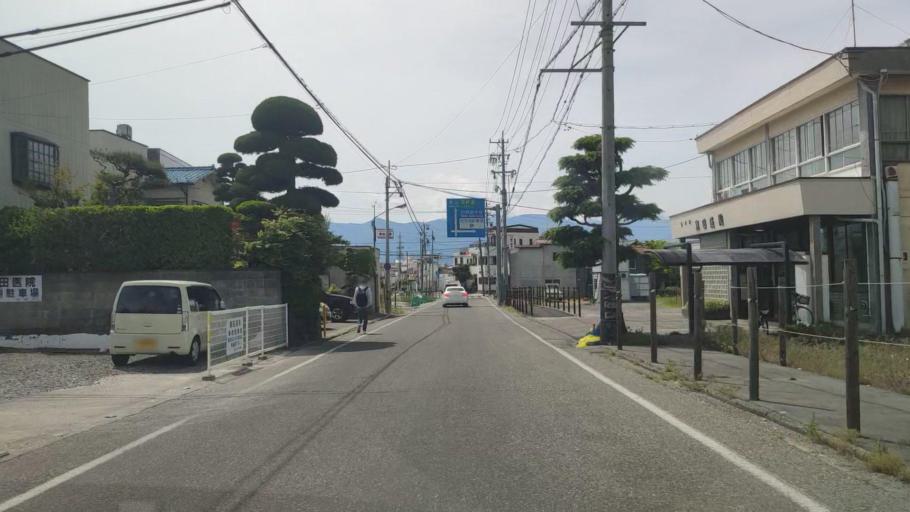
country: JP
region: Nagano
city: Matsumoto
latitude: 36.2372
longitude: 137.9688
